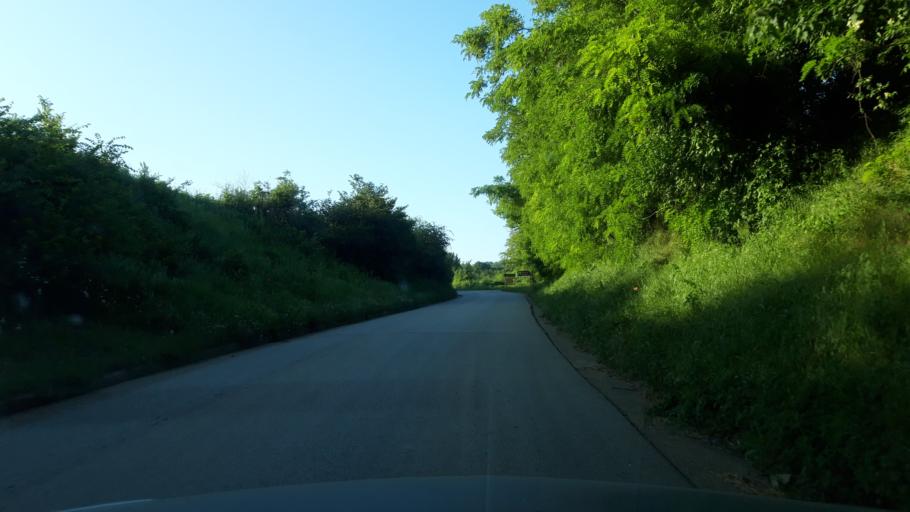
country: RS
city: Celarevo
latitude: 45.1236
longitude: 19.5081
